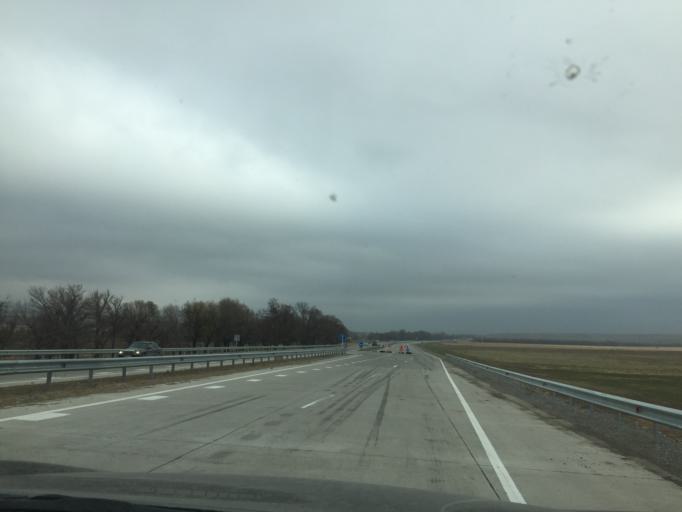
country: KZ
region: Ongtustik Qazaqstan
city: Kokterek
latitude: 42.5552
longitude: 70.1383
